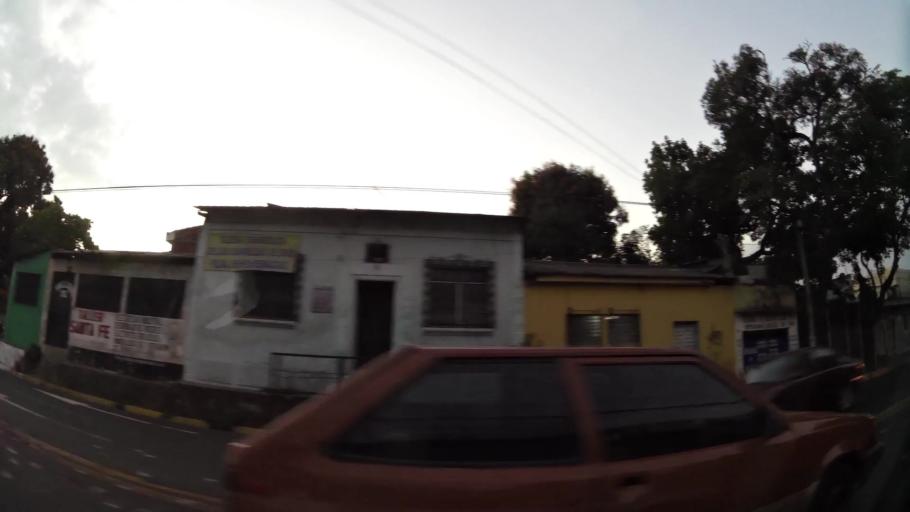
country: SV
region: San Salvador
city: Delgado
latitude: 13.7104
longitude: -89.1857
